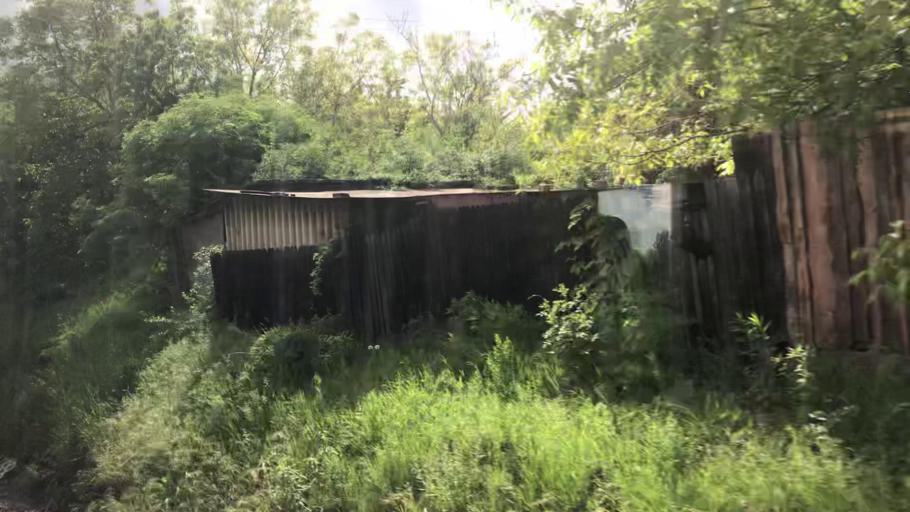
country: PL
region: Lower Silesian Voivodeship
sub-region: Powiat swidnicki
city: Swiebodzice
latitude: 50.8564
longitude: 16.3439
